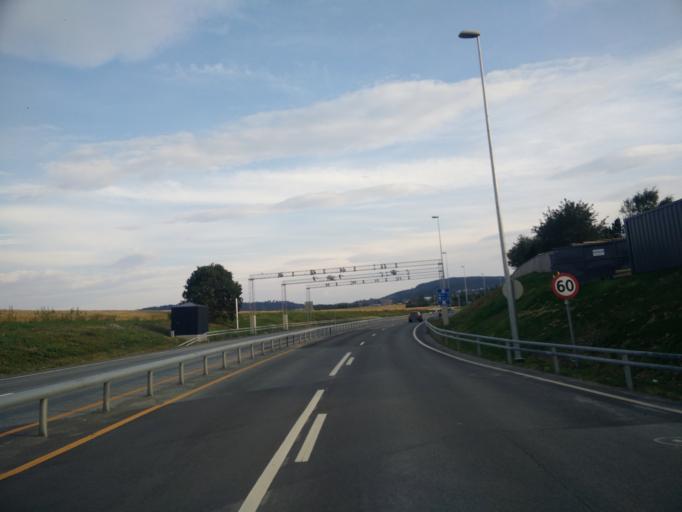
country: NO
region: Sor-Trondelag
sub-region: Trondheim
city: Trondheim
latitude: 63.4308
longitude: 10.4754
